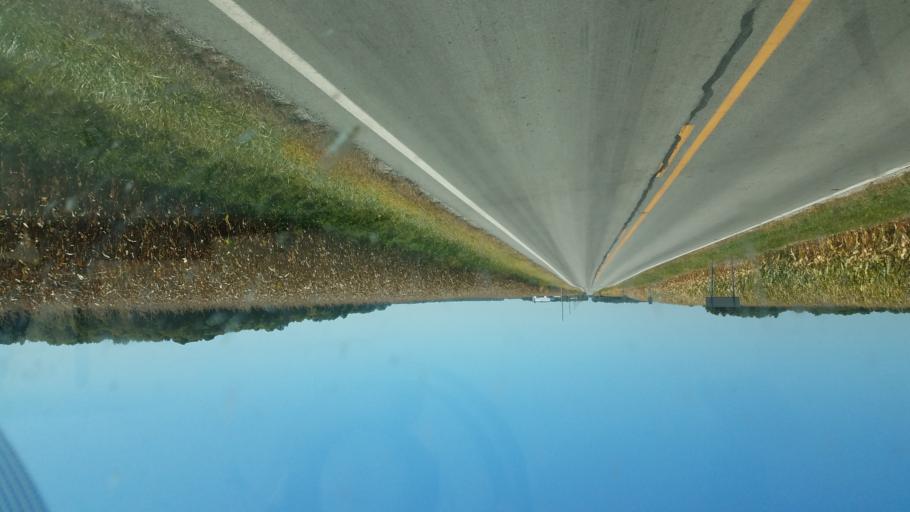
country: US
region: Ohio
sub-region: Crawford County
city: Bucyrus
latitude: 40.9503
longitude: -83.0156
